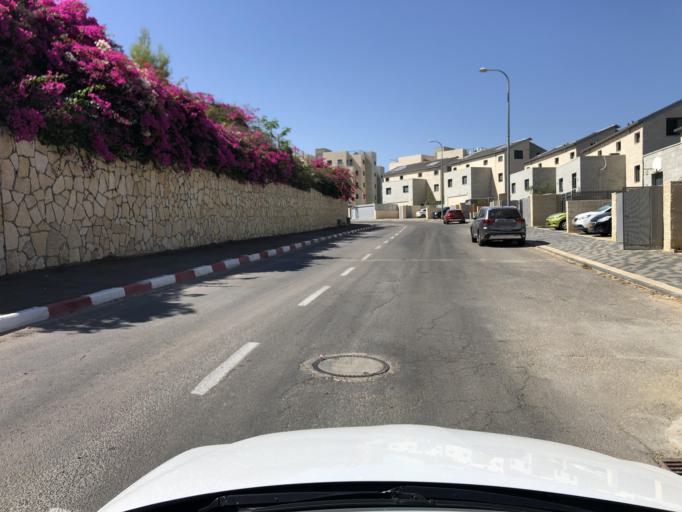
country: PS
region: West Bank
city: An Nabi Ilyas
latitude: 32.1649
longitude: 35.0233
